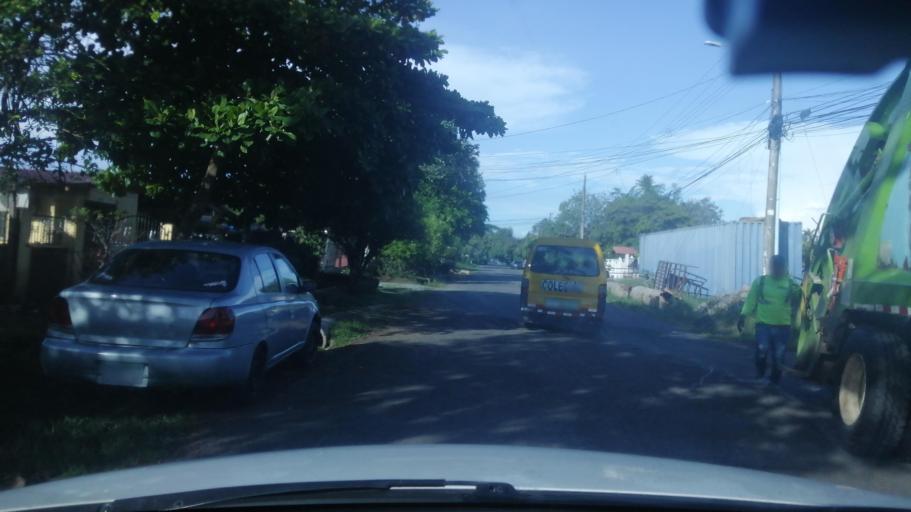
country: PA
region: Chiriqui
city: David
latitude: 8.4340
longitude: -82.4353
